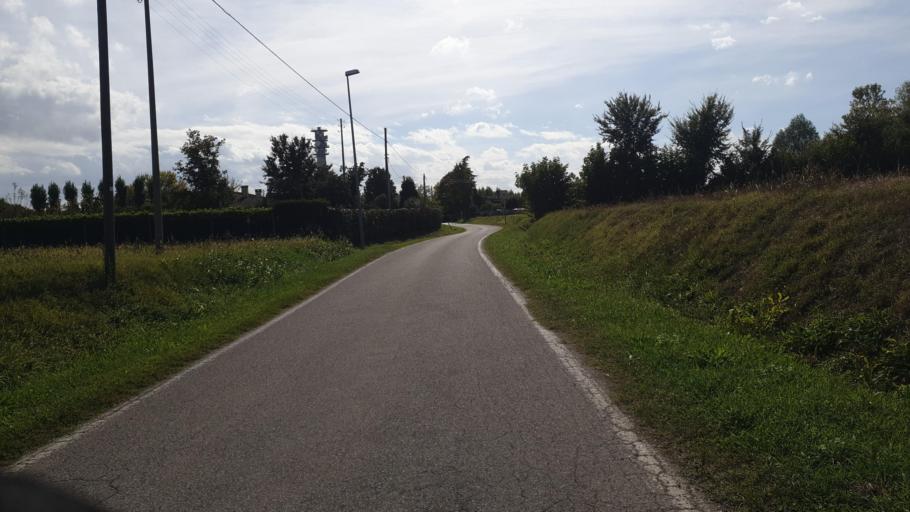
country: IT
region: Veneto
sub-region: Provincia di Padova
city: Arzergrande
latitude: 45.2788
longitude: 12.0550
